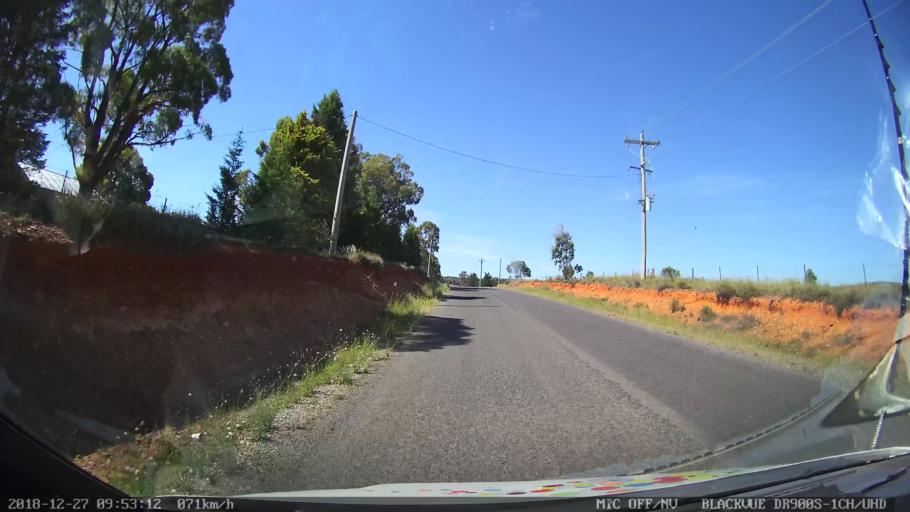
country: AU
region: New South Wales
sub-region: Lithgow
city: Portland
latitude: -33.3792
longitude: 149.9879
